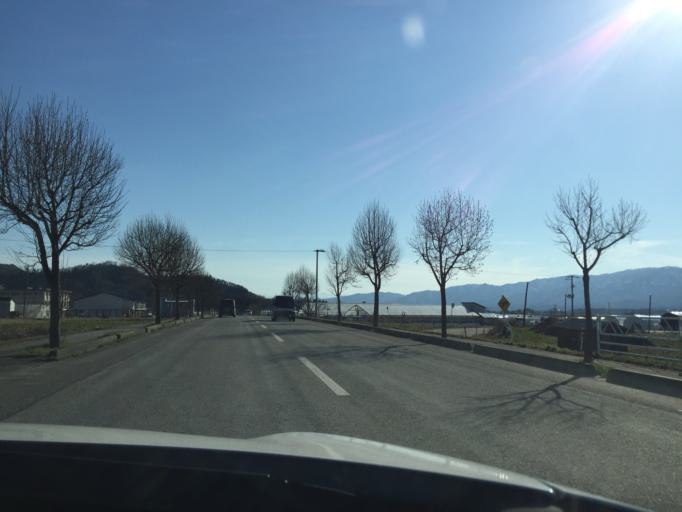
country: JP
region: Yamagata
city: Nagai
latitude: 38.1673
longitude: 140.0859
